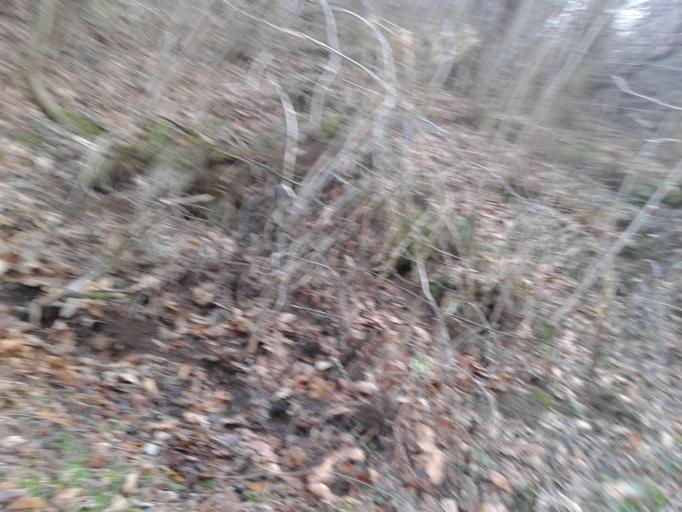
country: IT
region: Veneto
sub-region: Provincia di Vicenza
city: Monte di Malo
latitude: 45.6664
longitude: 11.3600
